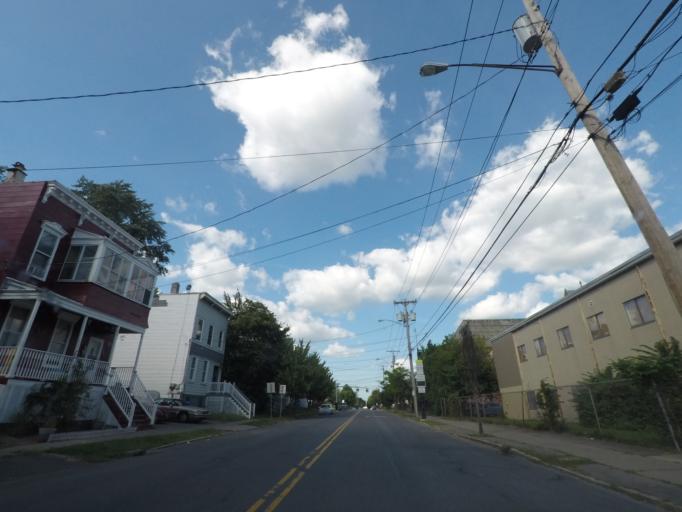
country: US
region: New York
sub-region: Albany County
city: Albany
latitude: 42.6716
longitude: -73.7405
